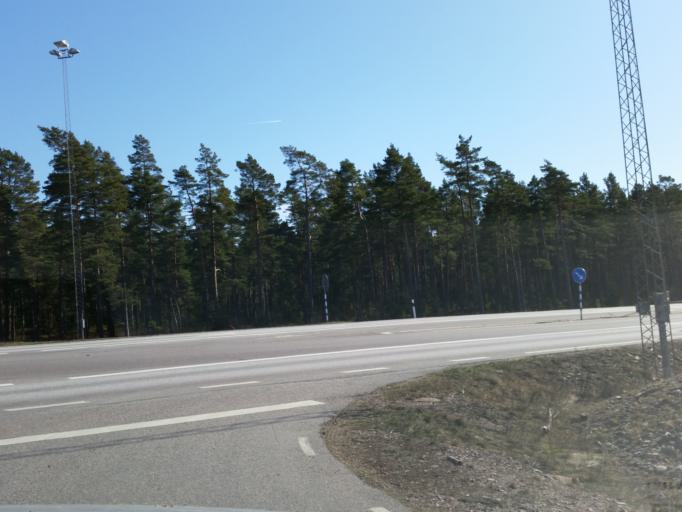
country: SE
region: Kalmar
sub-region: Monsteras Kommun
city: Moensteras
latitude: 57.0807
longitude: 16.4828
